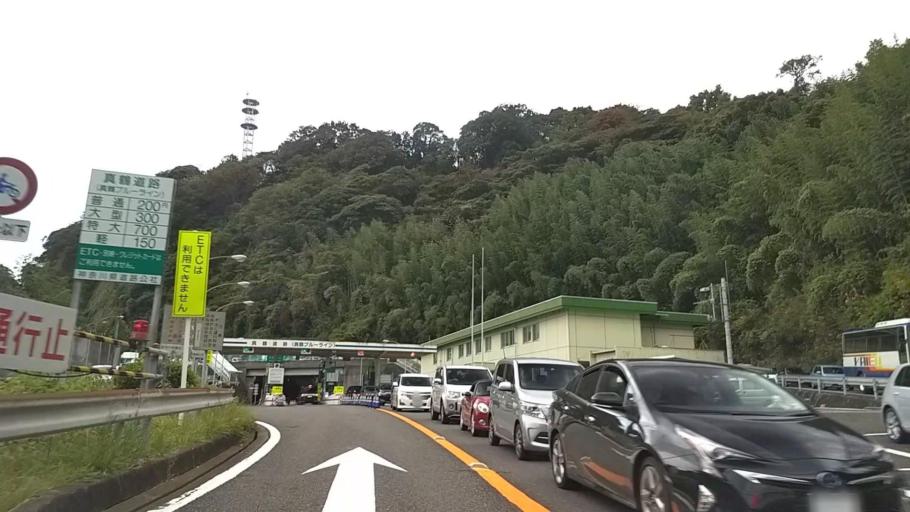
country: JP
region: Kanagawa
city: Yugawara
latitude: 35.1709
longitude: 139.1430
